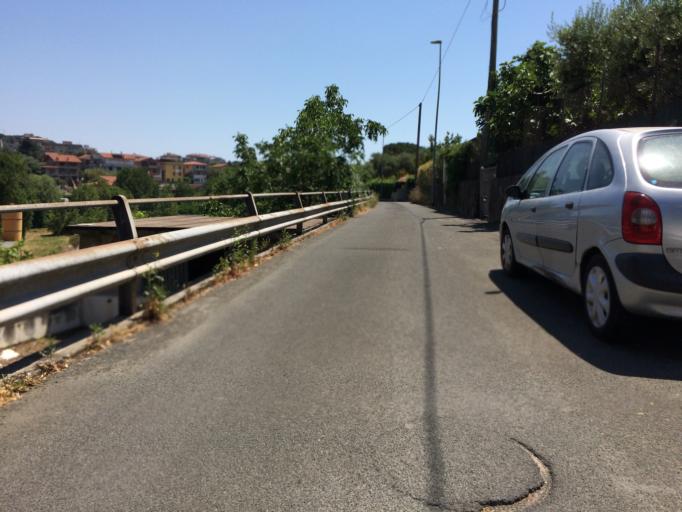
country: IT
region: Tuscany
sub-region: Provincia di Massa-Carrara
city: Massa
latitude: 44.0391
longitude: 10.1320
